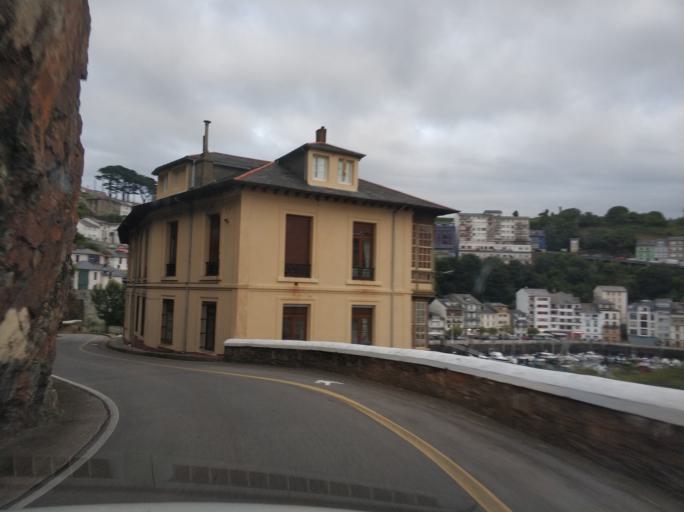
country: ES
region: Asturias
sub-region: Province of Asturias
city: Navia
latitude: 43.5471
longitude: -6.5336
